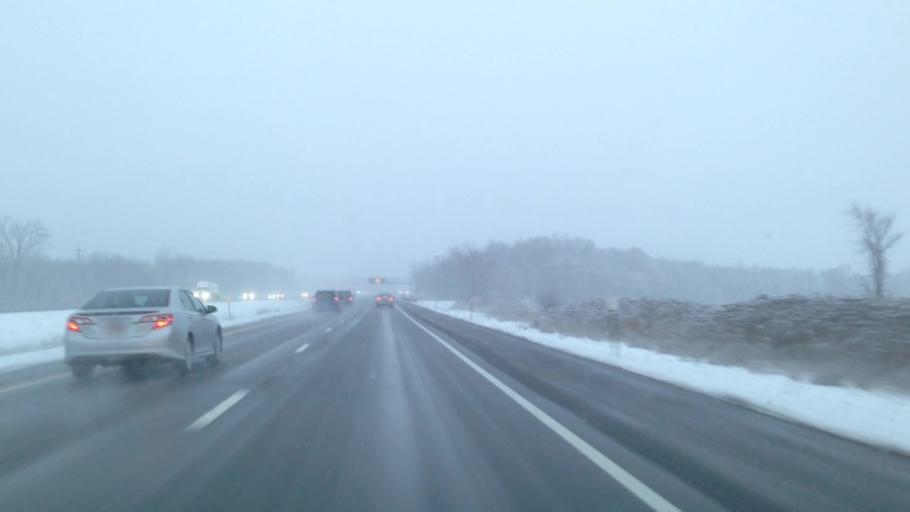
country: US
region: New York
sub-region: Madison County
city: Bolivar
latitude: 43.0956
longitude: -75.8532
